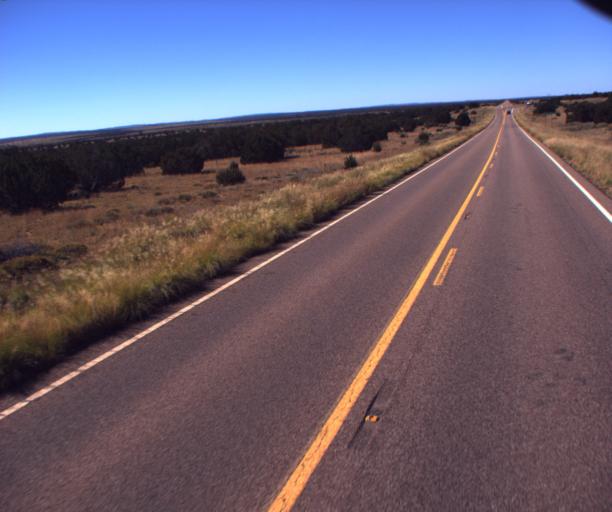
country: US
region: Arizona
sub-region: Navajo County
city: Taylor
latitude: 34.4824
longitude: -110.3340
